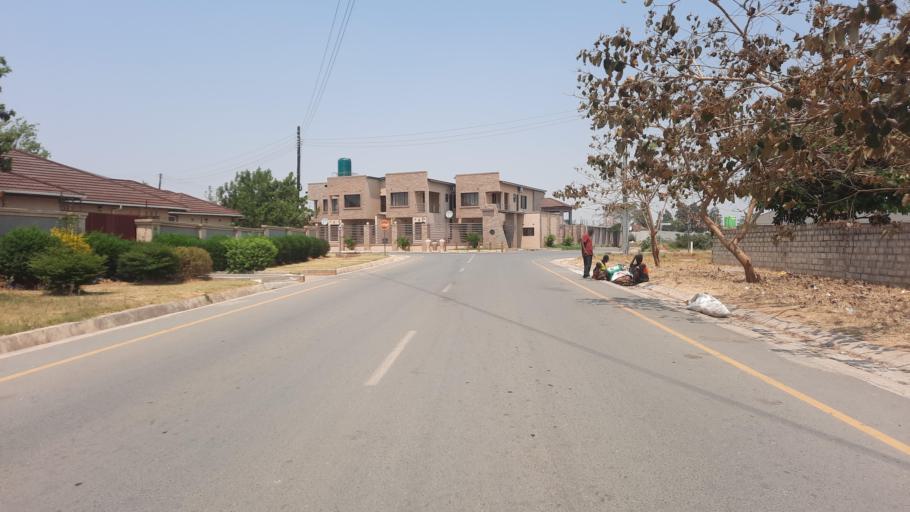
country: ZM
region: Lusaka
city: Lusaka
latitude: -15.3954
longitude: 28.3902
